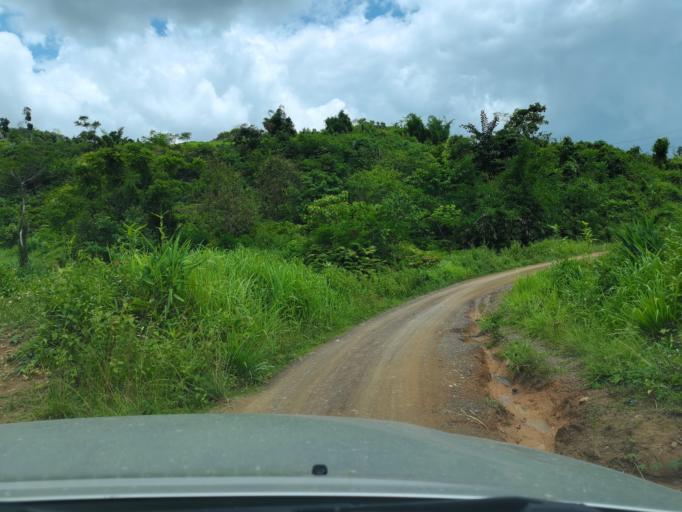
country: LA
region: Loungnamtha
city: Muang Long
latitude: 20.7333
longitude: 101.0145
